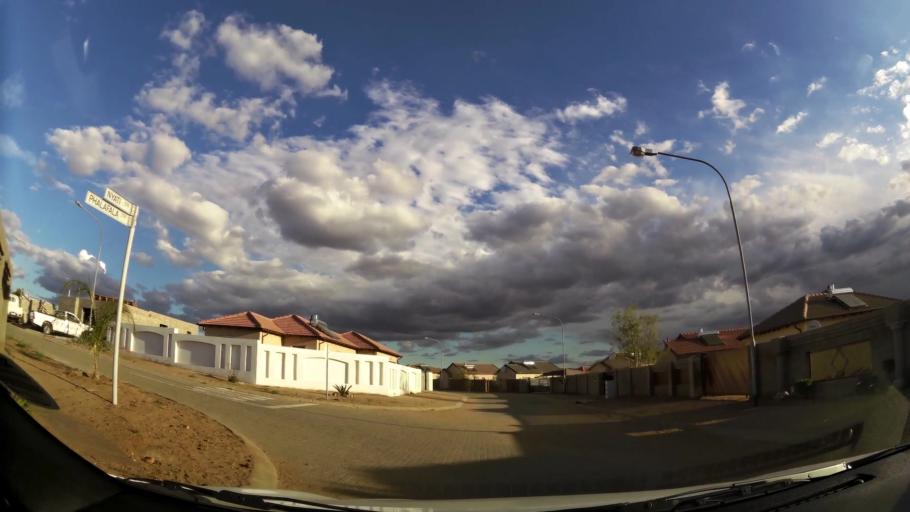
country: ZA
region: Limpopo
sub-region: Capricorn District Municipality
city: Polokwane
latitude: -23.9232
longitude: 29.4185
